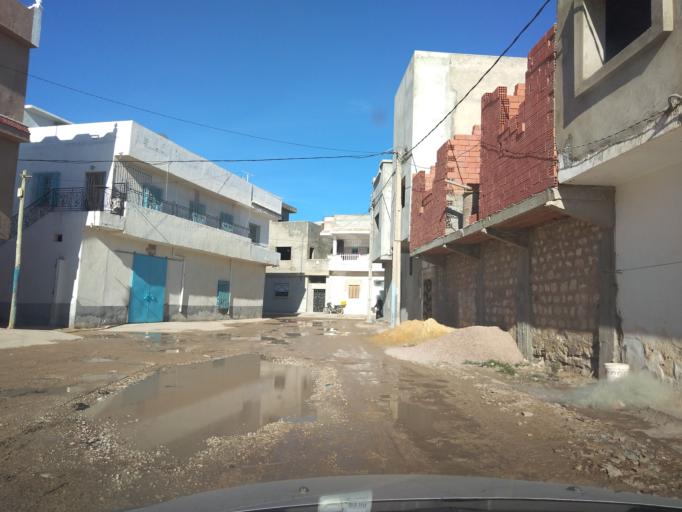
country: TN
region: Ariana
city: Qal'at al Andalus
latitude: 37.0631
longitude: 10.1219
